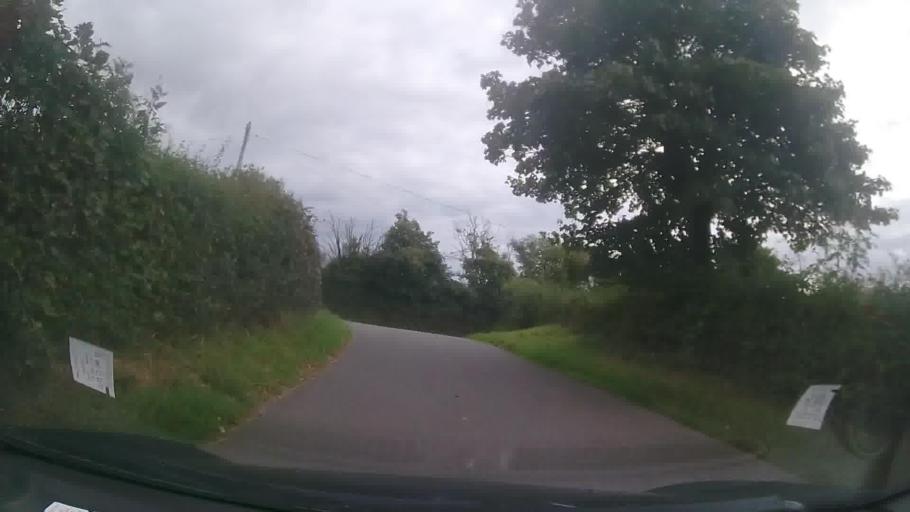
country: GB
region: Wales
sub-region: Pembrokeshire
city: Saundersfoot
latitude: 51.7410
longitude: -4.6622
